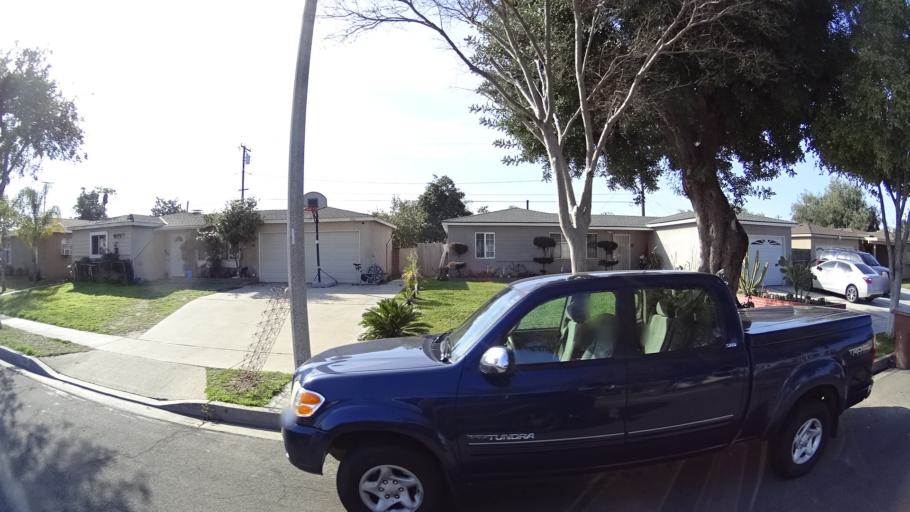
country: US
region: California
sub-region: Orange County
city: Fullerton
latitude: 33.8529
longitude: -117.9369
